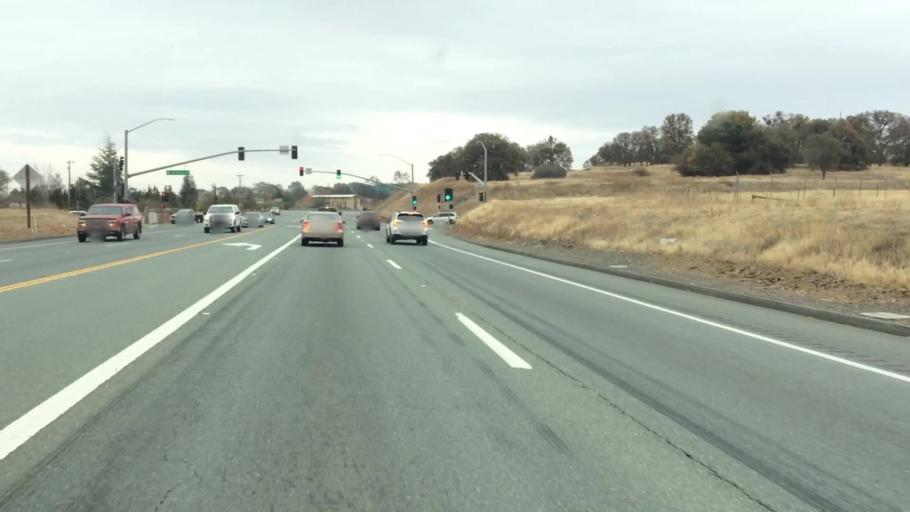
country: US
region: California
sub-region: Amador County
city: Sutter Creek
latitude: 38.3823
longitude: -120.8071
